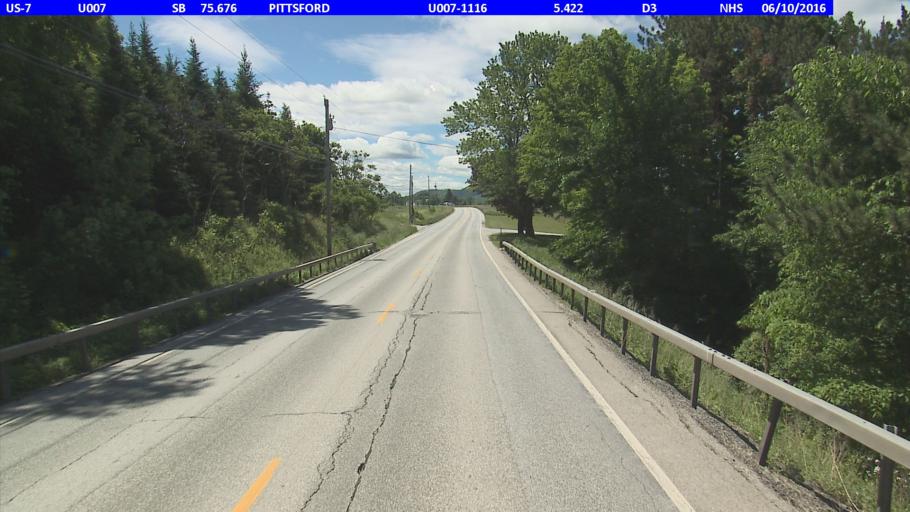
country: US
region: Vermont
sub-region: Rutland County
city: Brandon
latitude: 43.7256
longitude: -73.0387
